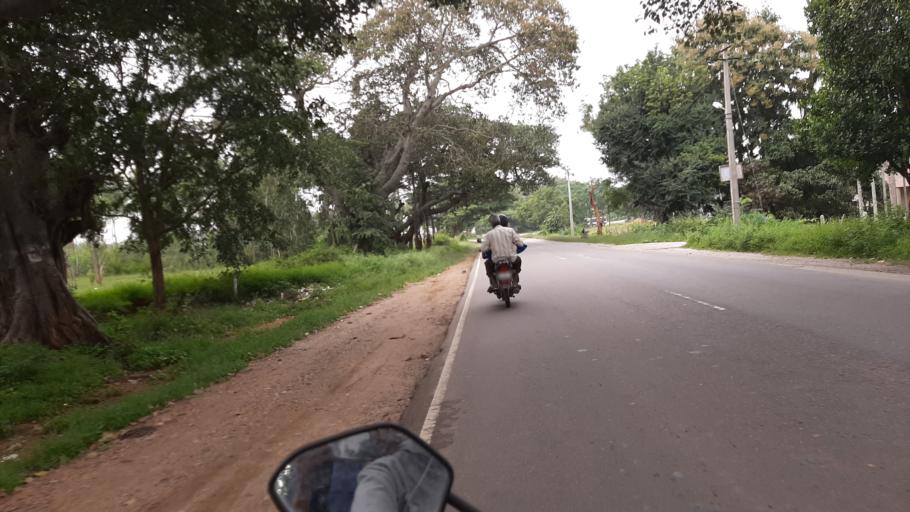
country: IN
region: Karnataka
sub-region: Bangalore Rural
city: Nelamangala
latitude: 12.9665
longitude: 77.3873
